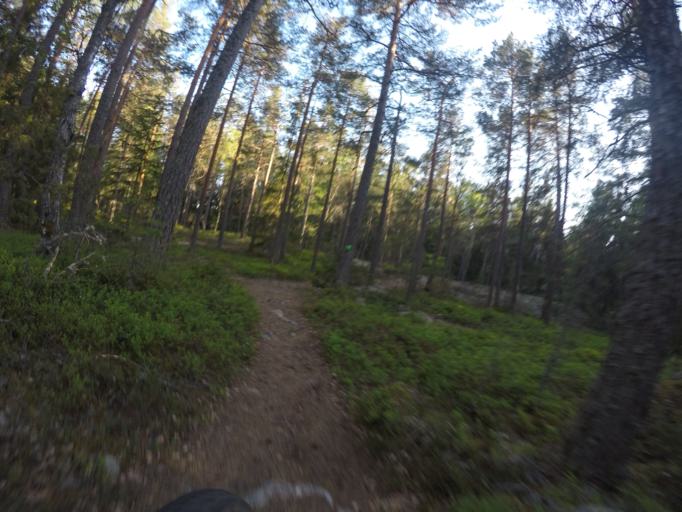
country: SE
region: Soedermanland
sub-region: Eskilstuna Kommun
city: Eskilstuna
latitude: 59.3359
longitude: 16.5222
